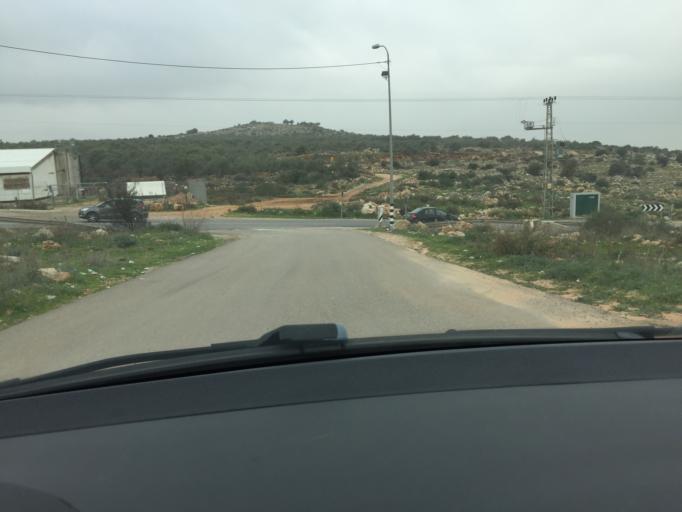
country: PS
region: West Bank
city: Al Lubban al Gharbi
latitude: 32.0448
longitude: 35.0424
